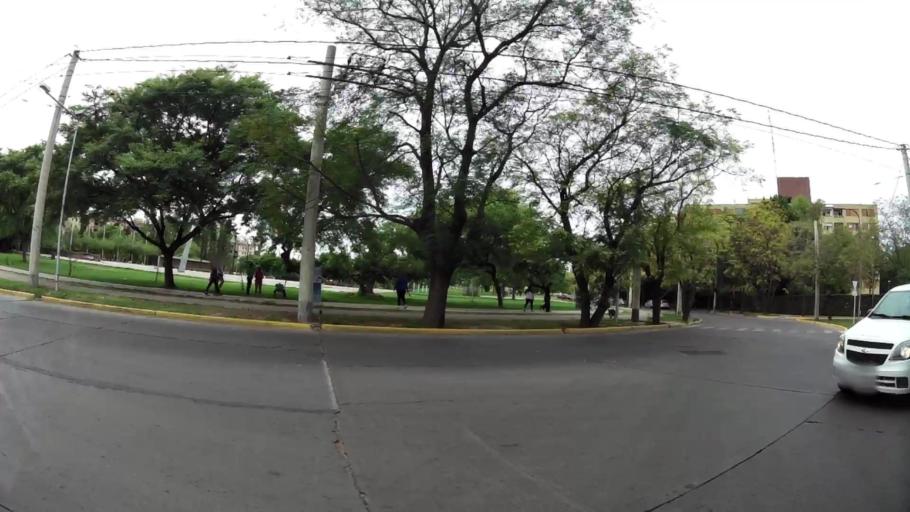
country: AR
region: Mendoza
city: Mendoza
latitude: -32.8731
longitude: -68.8435
